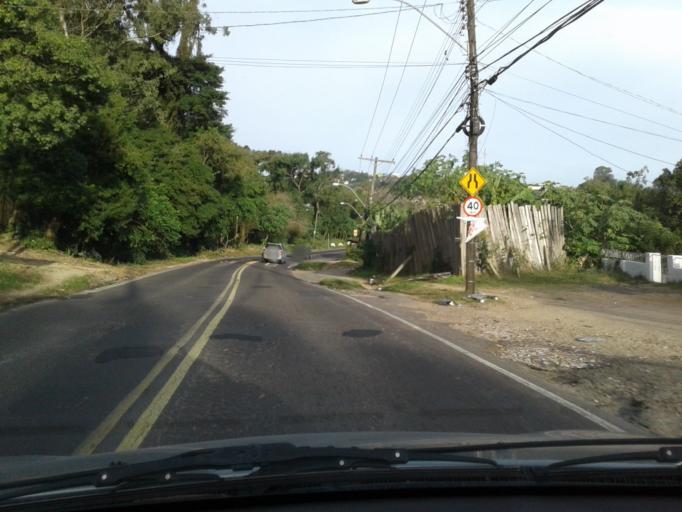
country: BR
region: Rio Grande do Sul
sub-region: Porto Alegre
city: Porto Alegre
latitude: -30.1011
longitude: -51.2246
